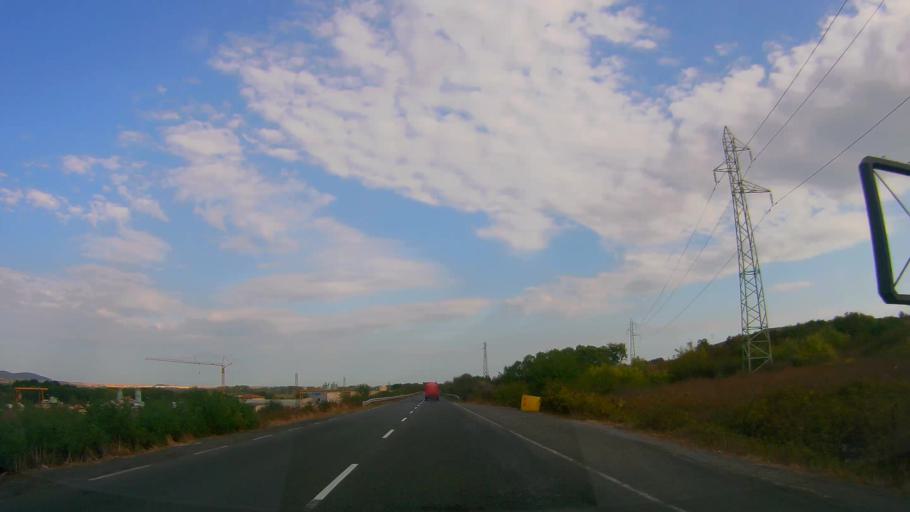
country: BG
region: Burgas
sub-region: Obshtina Sozopol
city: Sozopol
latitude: 42.3928
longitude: 27.6764
